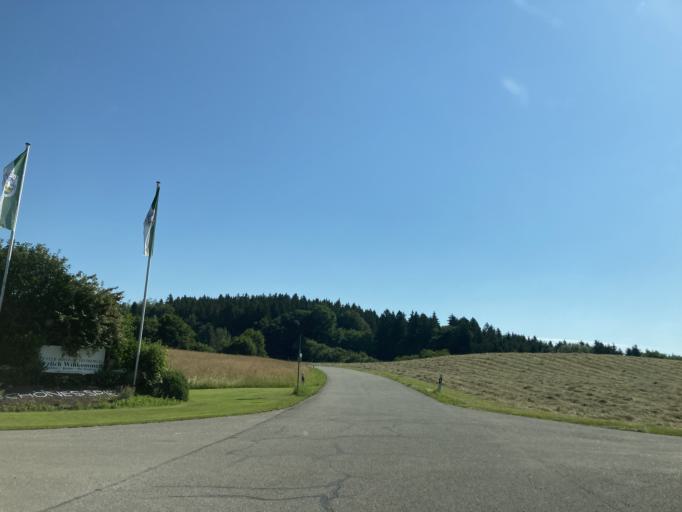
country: DE
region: Bavaria
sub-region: Upper Bavaria
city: Hoslwang
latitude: 47.9648
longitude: 12.3370
